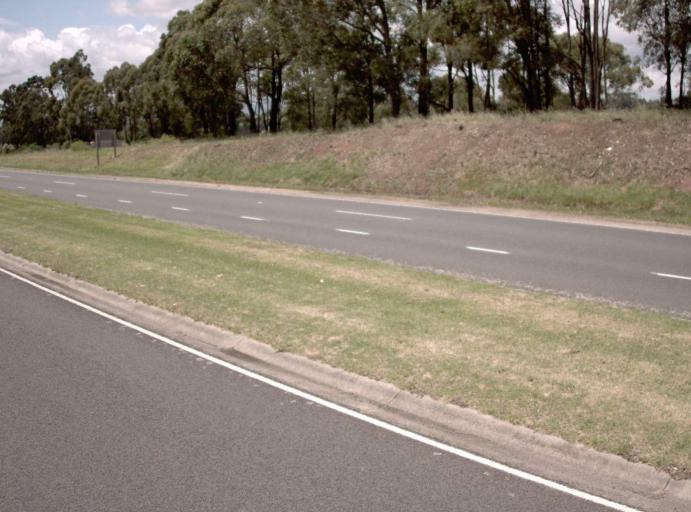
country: AU
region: Victoria
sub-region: Baw Baw
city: Warragul
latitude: -38.1420
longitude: 145.8875
